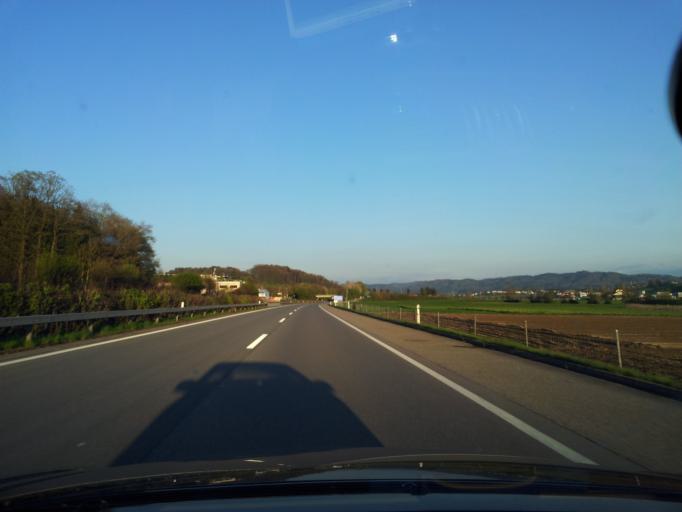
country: CH
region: Bern
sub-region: Bern-Mittelland District
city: Munchenbuchsee
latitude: 47.0400
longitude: 7.4214
